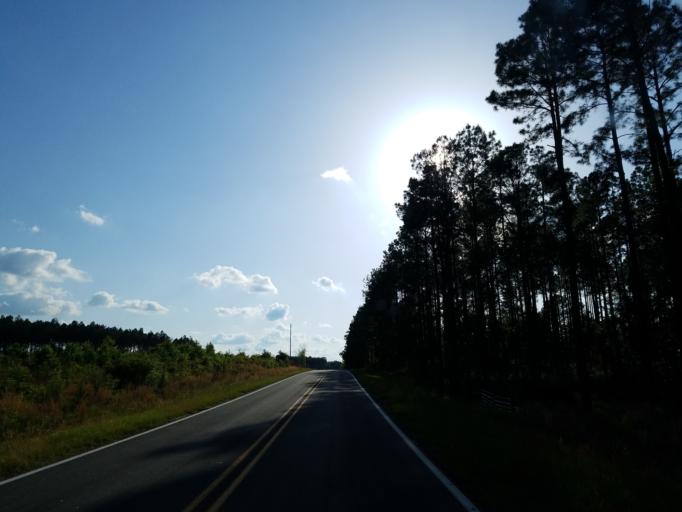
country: US
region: Georgia
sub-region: Turner County
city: Ashburn
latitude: 31.6092
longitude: -83.5799
